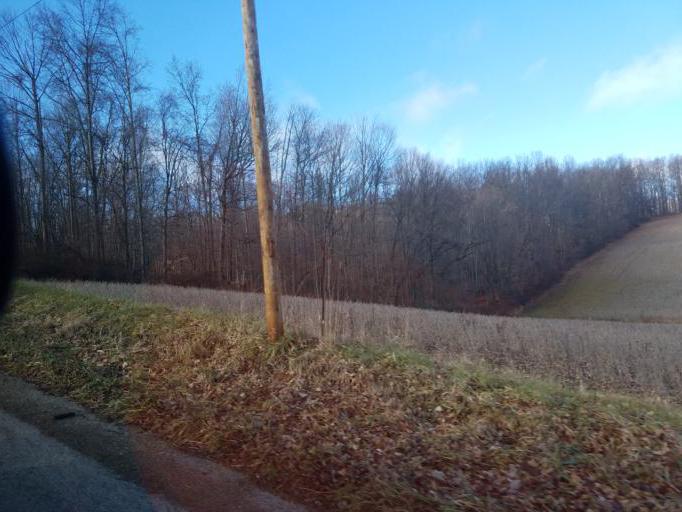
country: US
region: Ohio
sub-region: Sandusky County
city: Bellville
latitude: 40.5829
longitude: -82.5370
